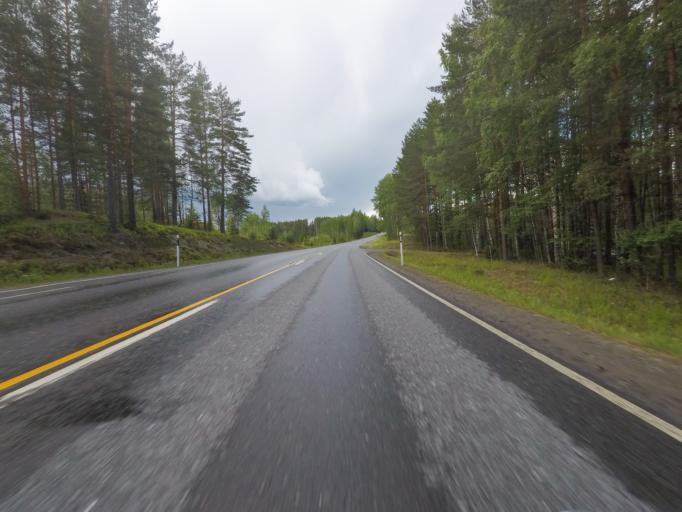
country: FI
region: Paijanne Tavastia
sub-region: Lahti
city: Hartola
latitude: 61.6438
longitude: 26.0266
